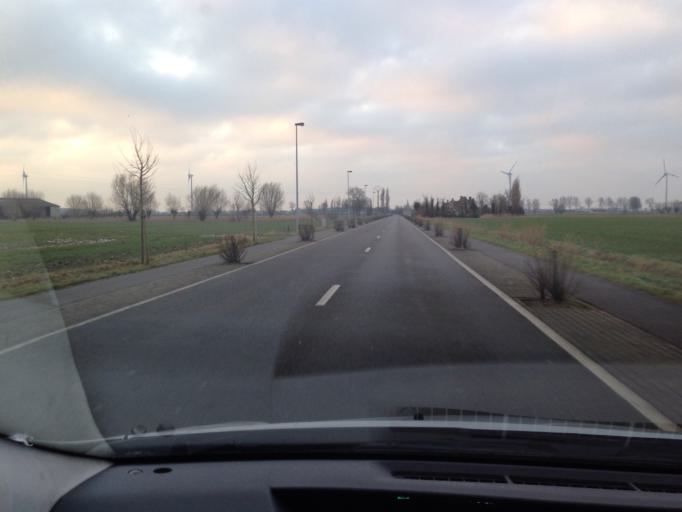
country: BE
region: Flanders
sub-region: Provincie West-Vlaanderen
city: Gistel
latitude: 51.1792
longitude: 2.9625
